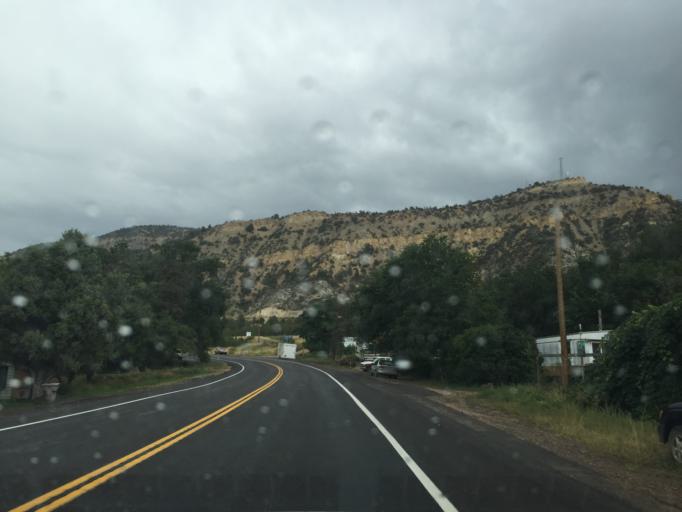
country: US
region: Utah
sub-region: Kane County
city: Kanab
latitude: 37.2759
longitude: -112.6333
